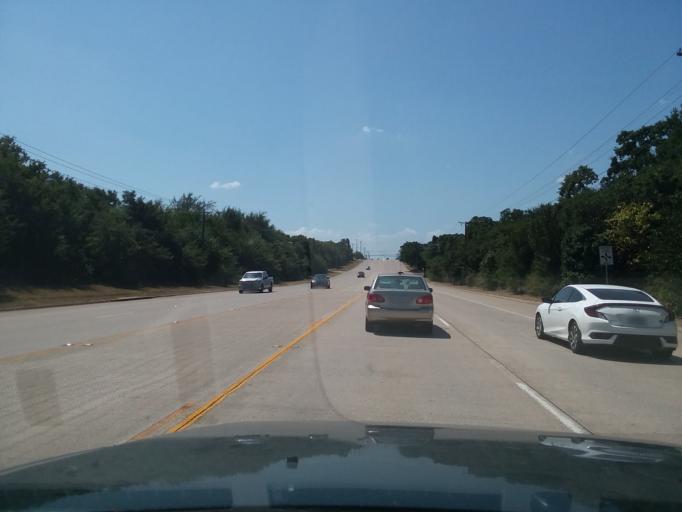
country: US
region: Texas
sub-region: Tarrant County
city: Euless
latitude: 32.8577
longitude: -97.1000
